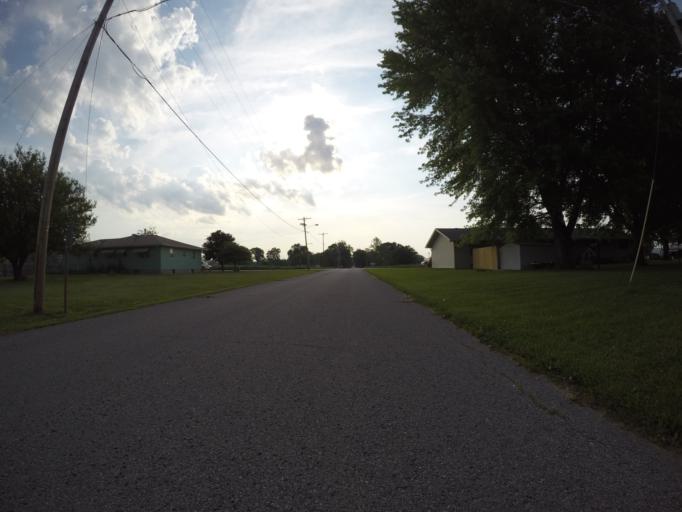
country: US
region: Kansas
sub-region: Doniphan County
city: Elwood
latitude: 39.7518
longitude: -94.8799
